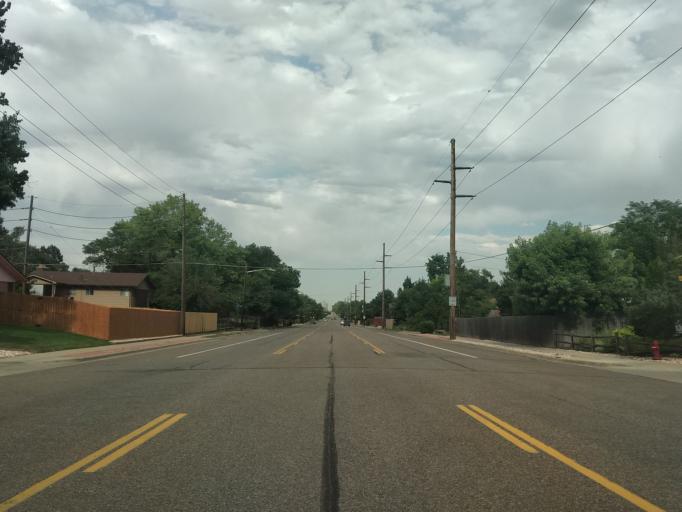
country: US
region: Colorado
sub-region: Jefferson County
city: Lakewood
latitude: 39.6966
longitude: -105.1087
